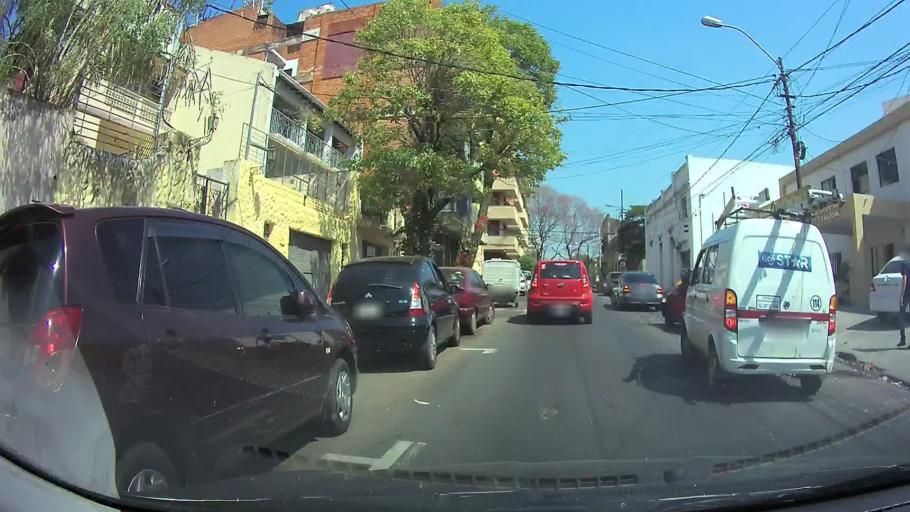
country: PY
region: Asuncion
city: Asuncion
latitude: -25.2889
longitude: -57.6389
